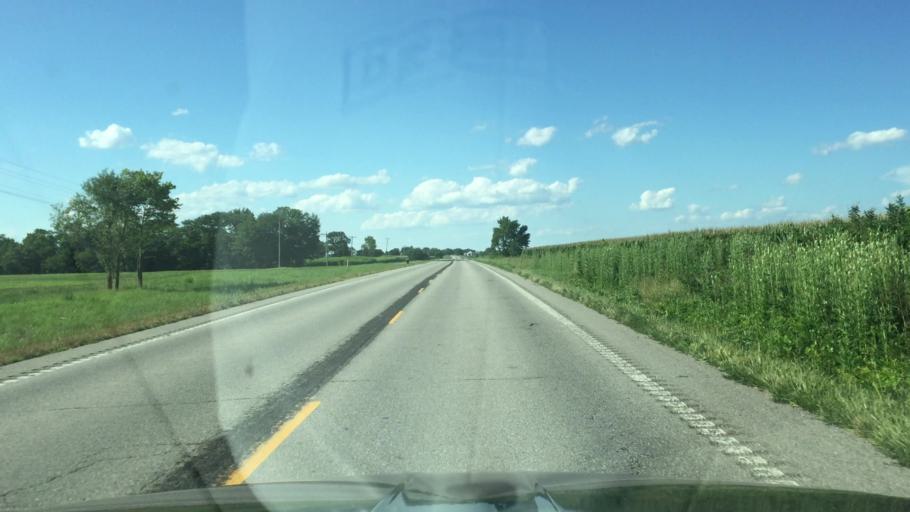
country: US
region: Missouri
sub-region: Moniteau County
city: Tipton
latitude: 38.5926
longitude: -92.7891
